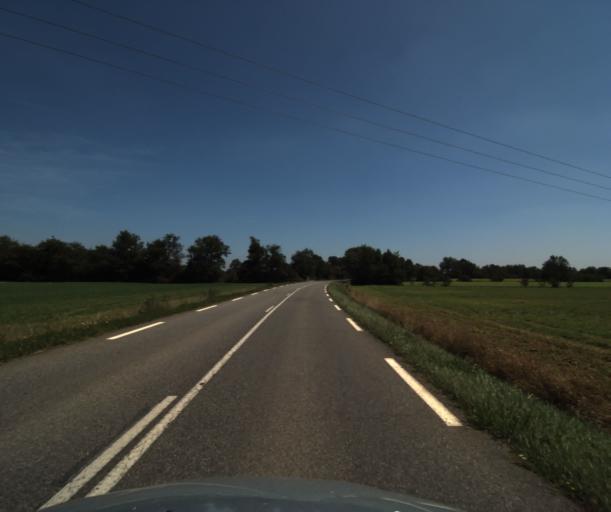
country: FR
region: Midi-Pyrenees
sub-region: Departement de la Haute-Garonne
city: Fonsorbes
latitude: 43.5087
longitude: 1.2328
